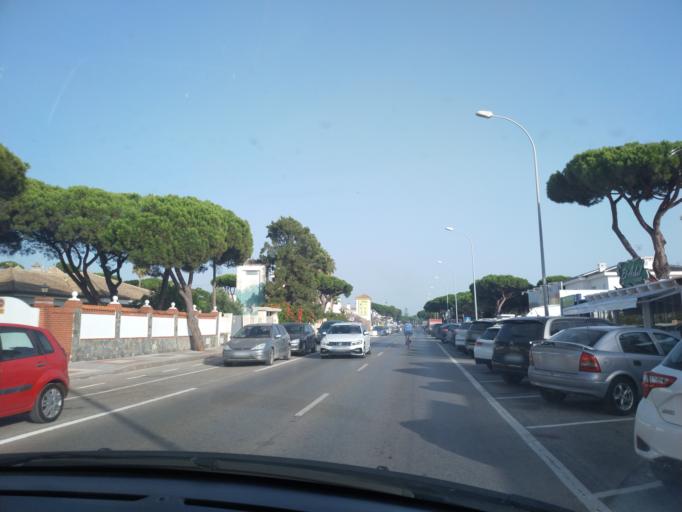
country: ES
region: Andalusia
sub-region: Provincia de Cadiz
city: Chiclana de la Frontera
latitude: 36.3727
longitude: -6.1827
